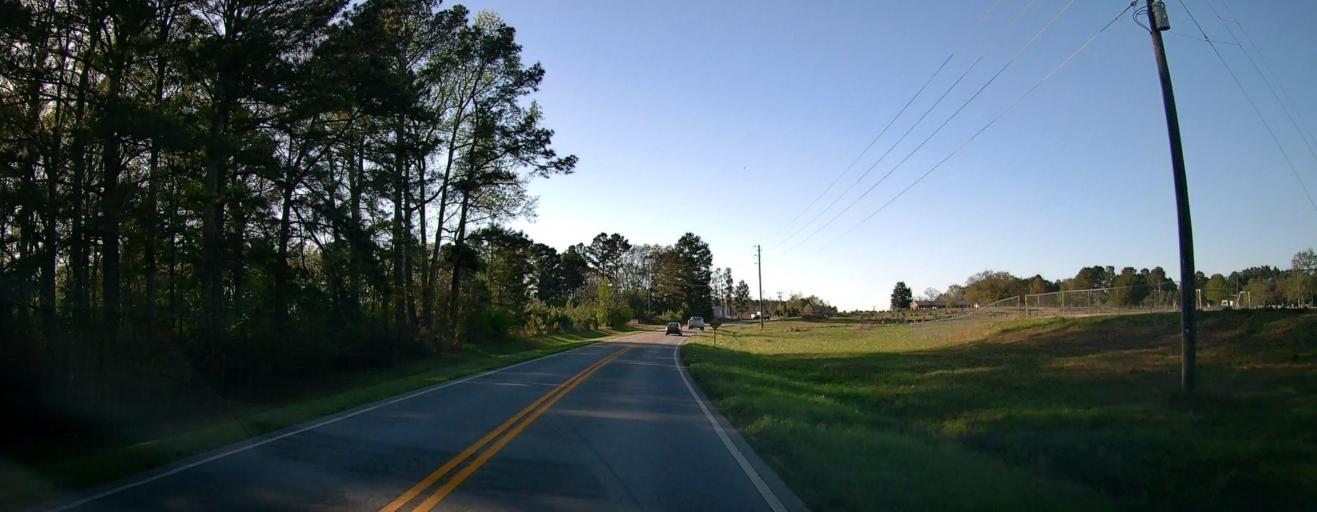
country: US
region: Georgia
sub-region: Butts County
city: Jackson
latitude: 33.3286
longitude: -83.9059
